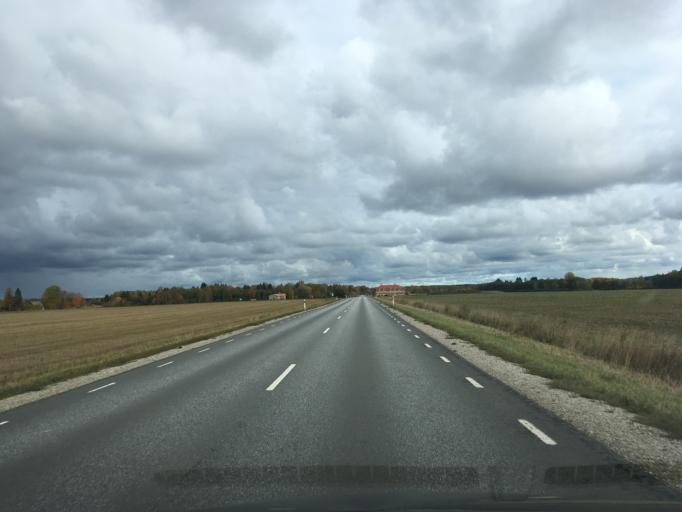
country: EE
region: Harju
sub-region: Anija vald
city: Kehra
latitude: 59.2751
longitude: 25.3616
